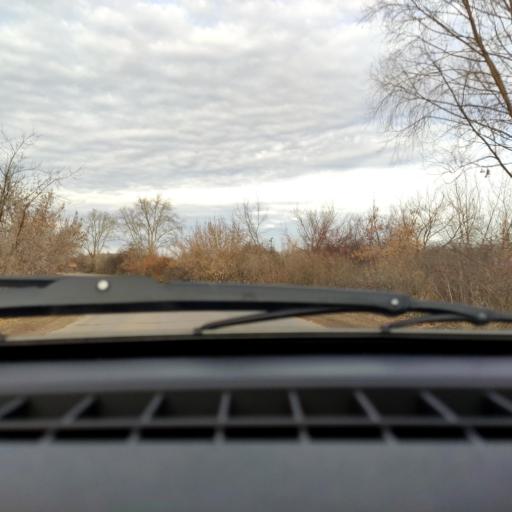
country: RU
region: Bashkortostan
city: Ufa
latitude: 54.8688
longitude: 56.1320
